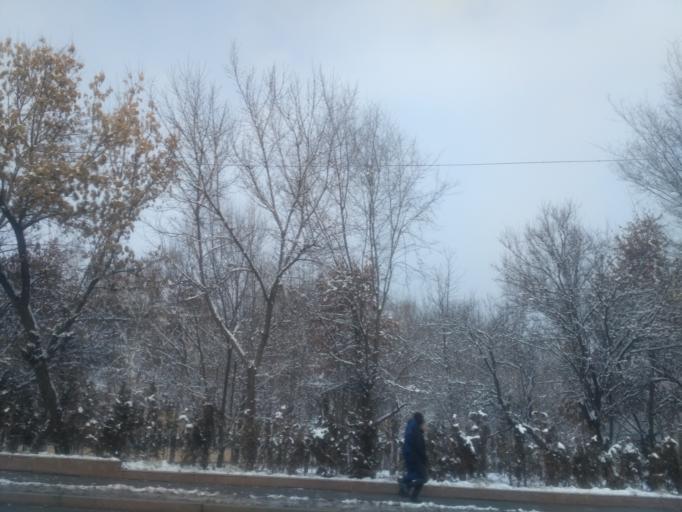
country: KZ
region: Almaty Qalasy
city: Almaty
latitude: 43.2161
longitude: 76.9256
